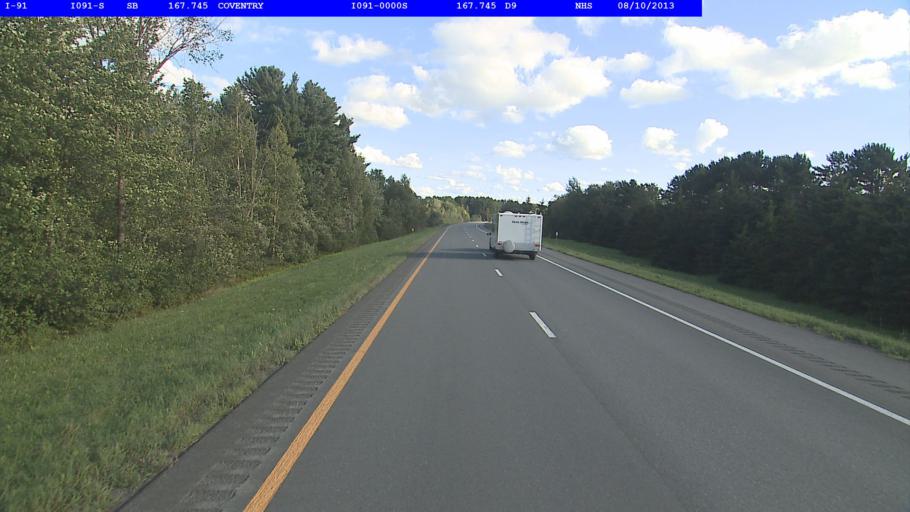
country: US
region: Vermont
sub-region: Orleans County
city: Newport
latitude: 44.8904
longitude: -72.1733
